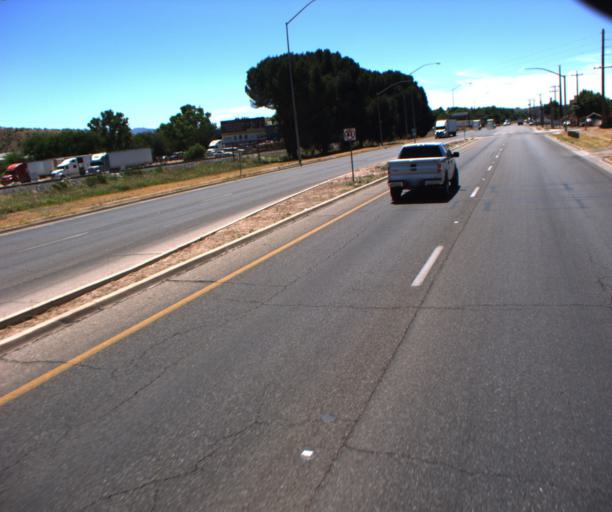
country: US
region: Arizona
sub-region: Santa Cruz County
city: Nogales
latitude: 31.3806
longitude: -110.9441
